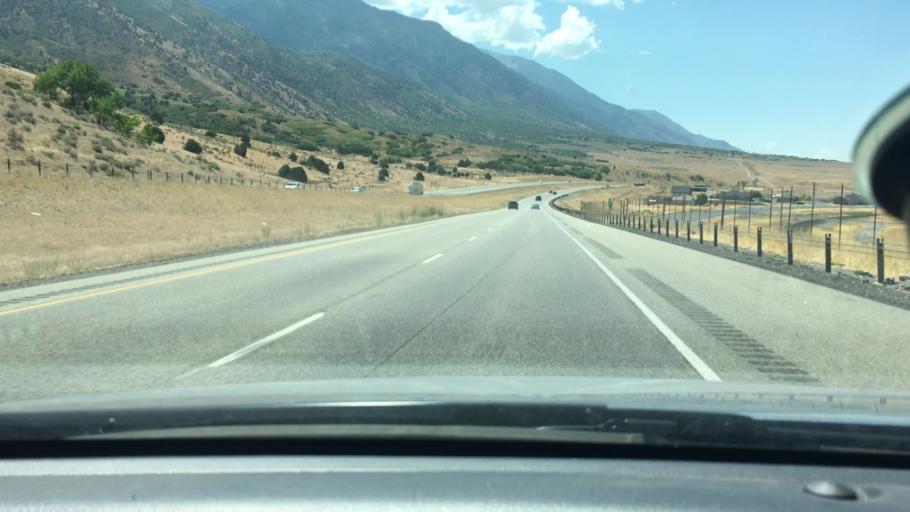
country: US
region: Utah
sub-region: Utah County
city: Santaquin
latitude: 39.9327
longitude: -111.8122
